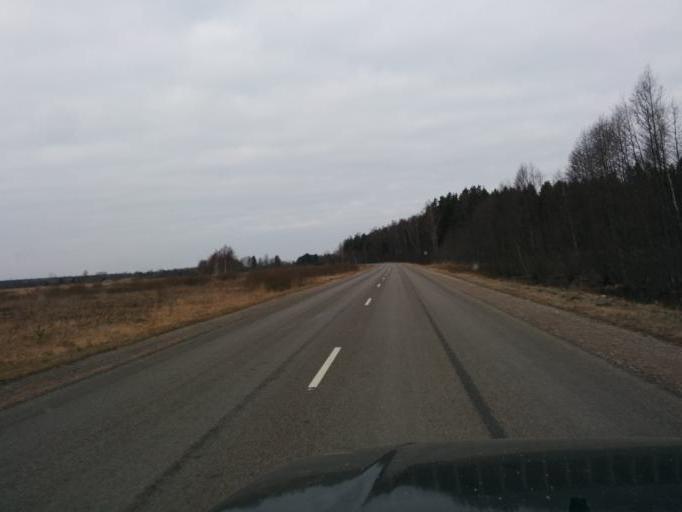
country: LV
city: Tireli
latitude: 56.8289
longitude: 23.6036
